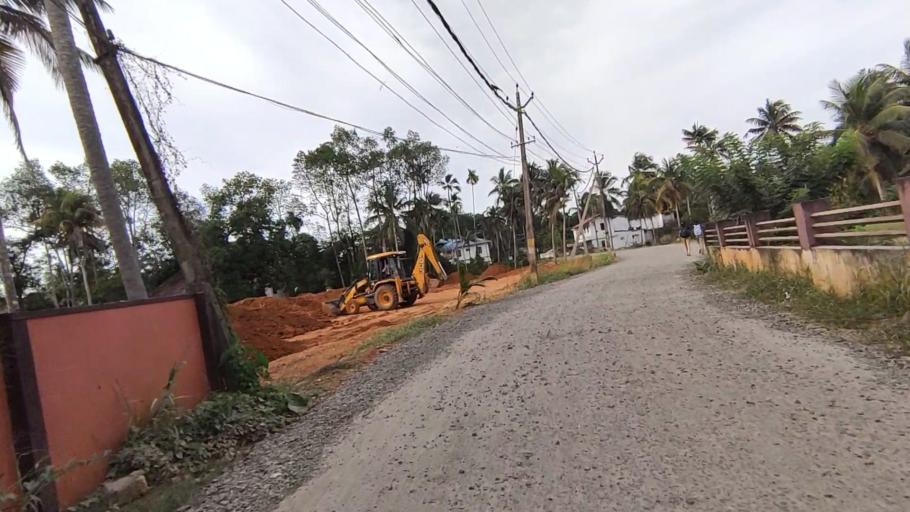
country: IN
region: Kerala
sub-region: Kottayam
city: Kottayam
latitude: 9.5871
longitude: 76.4921
